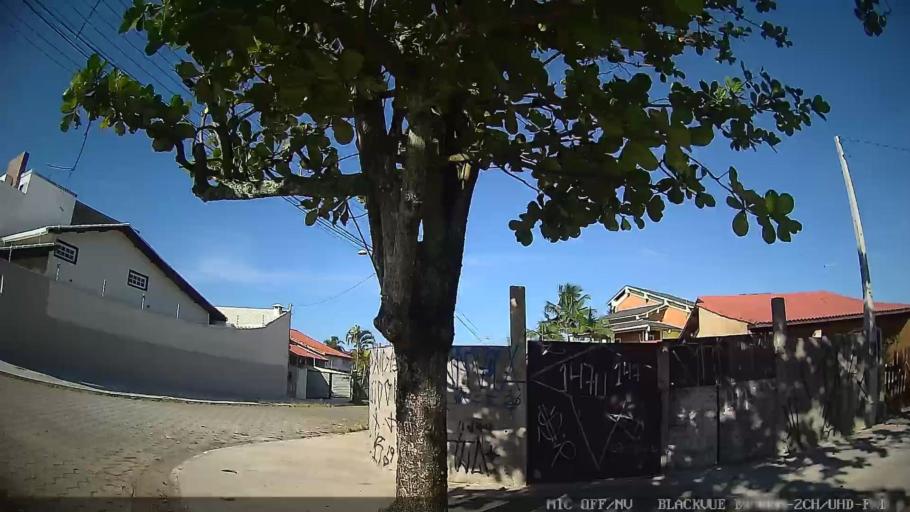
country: BR
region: Sao Paulo
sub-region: Peruibe
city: Peruibe
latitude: -24.2836
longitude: -46.9489
